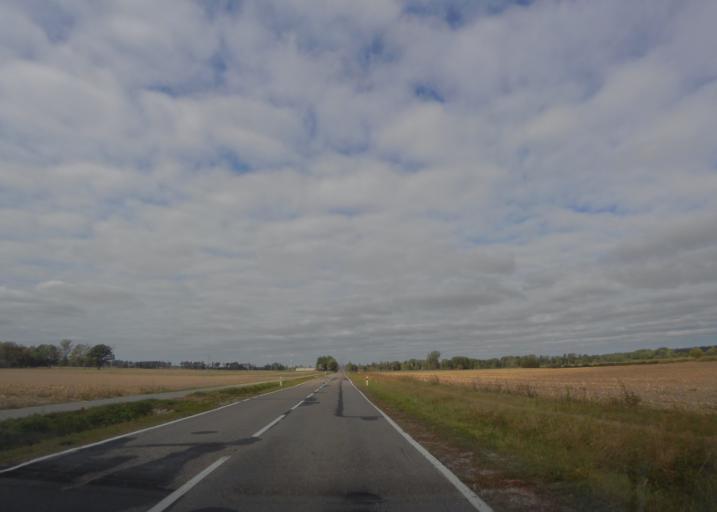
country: PL
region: Lublin Voivodeship
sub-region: Powiat bialski
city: Slawatycze
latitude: 51.6599
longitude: 23.5194
